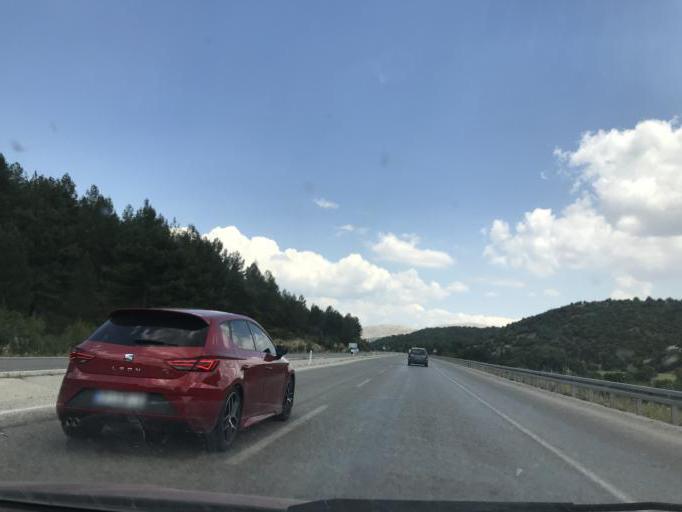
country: TR
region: Denizli
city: Tavas
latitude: 37.6140
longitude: 29.1487
